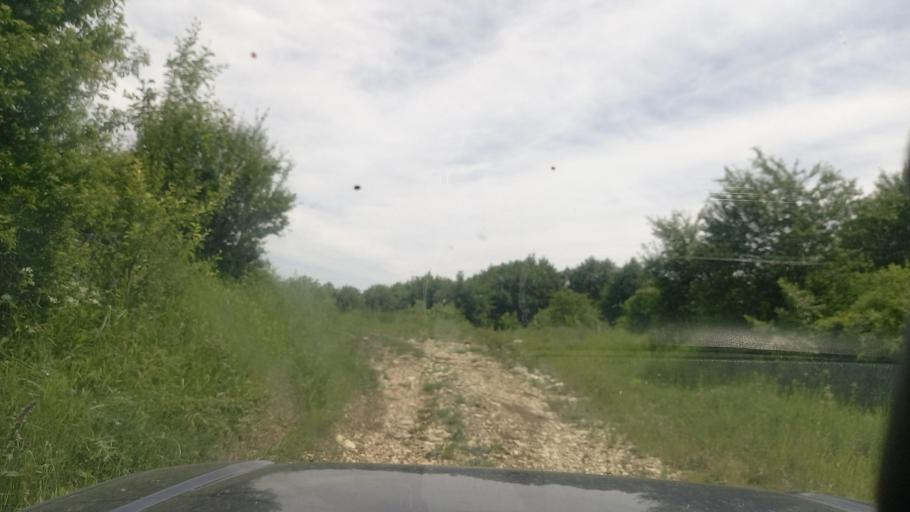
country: RU
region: Karachayevo-Cherkesiya
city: Pregradnaya
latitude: 44.0931
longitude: 41.1340
